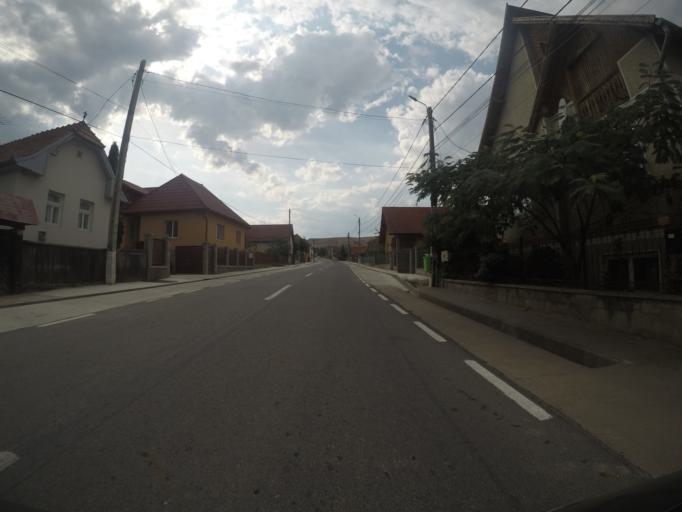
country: RO
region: Cluj
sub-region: Comuna Sandulesti
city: Sandulesti
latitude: 46.5801
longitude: 23.7257
